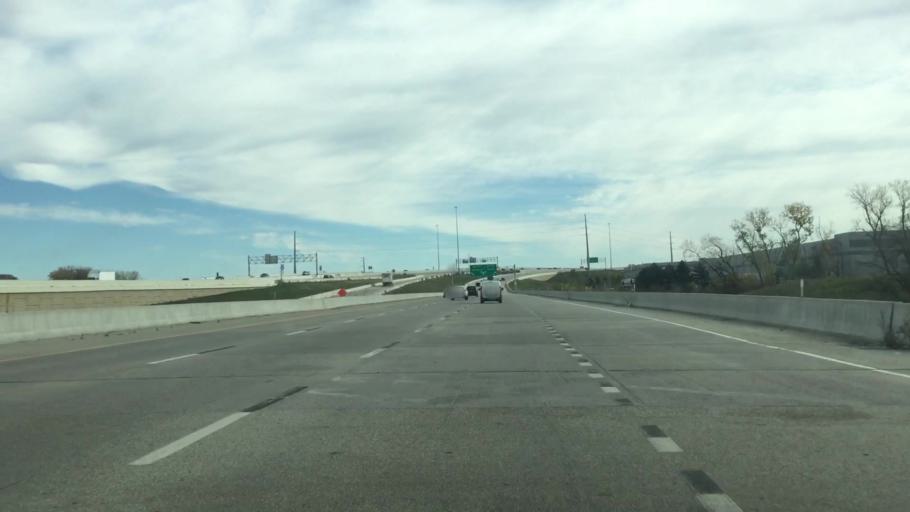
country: US
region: Kansas
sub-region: Johnson County
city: Lenexa
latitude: 38.9417
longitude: -94.7605
